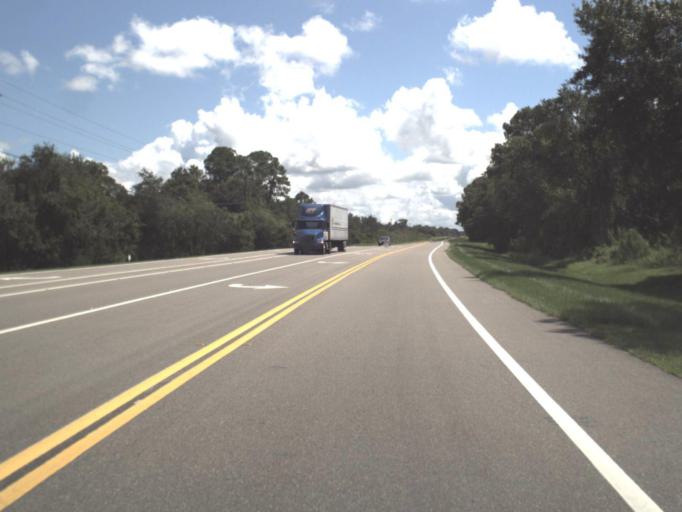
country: US
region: Florida
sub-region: Sarasota County
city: The Meadows
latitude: 27.4024
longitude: -82.3120
